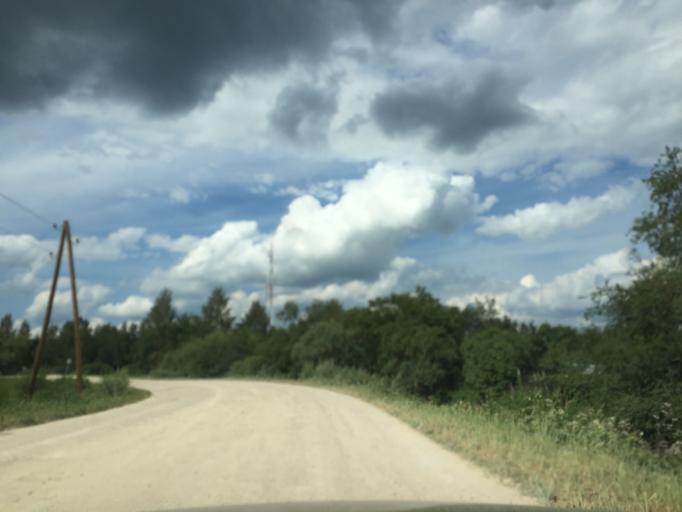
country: LV
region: Jelgava
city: Jelgava
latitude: 56.6398
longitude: 23.6142
